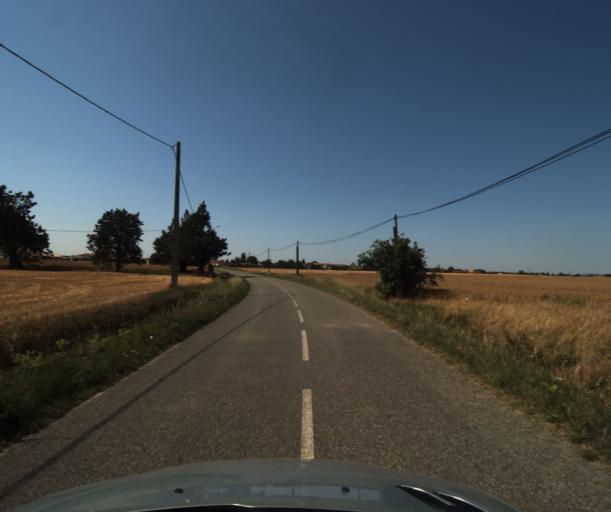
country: FR
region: Midi-Pyrenees
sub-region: Departement de la Haute-Garonne
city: Labarthe-sur-Leze
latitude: 43.4647
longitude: 1.3792
